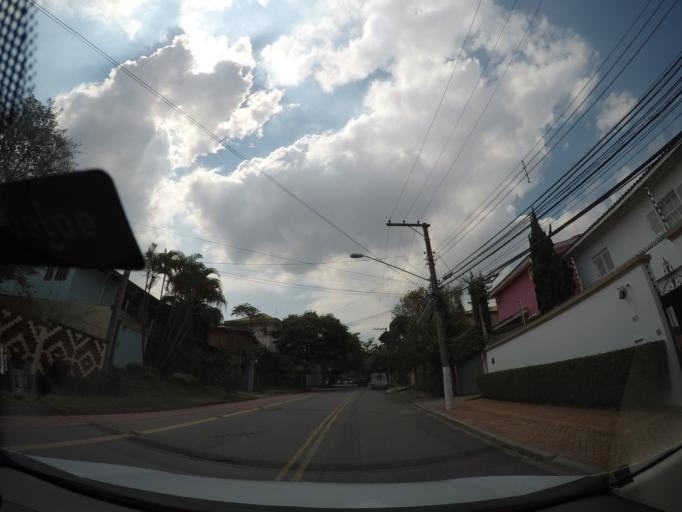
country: BR
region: Sao Paulo
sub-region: Sao Paulo
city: Sao Paulo
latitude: -23.6016
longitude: -46.7032
